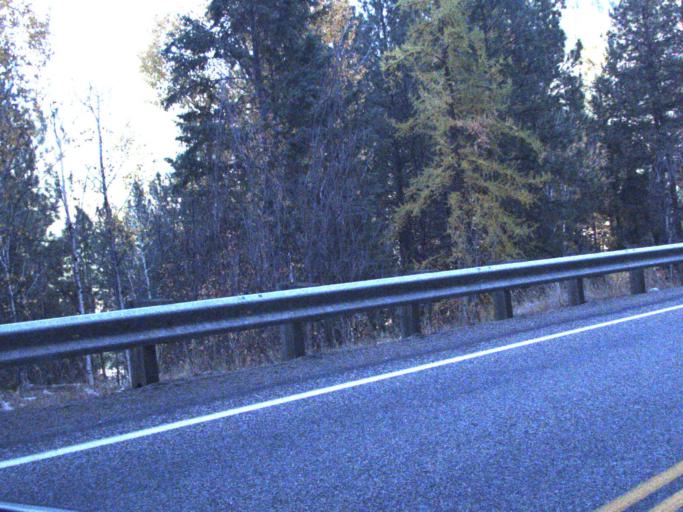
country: CA
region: British Columbia
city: Rossland
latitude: 48.8736
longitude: -117.8482
